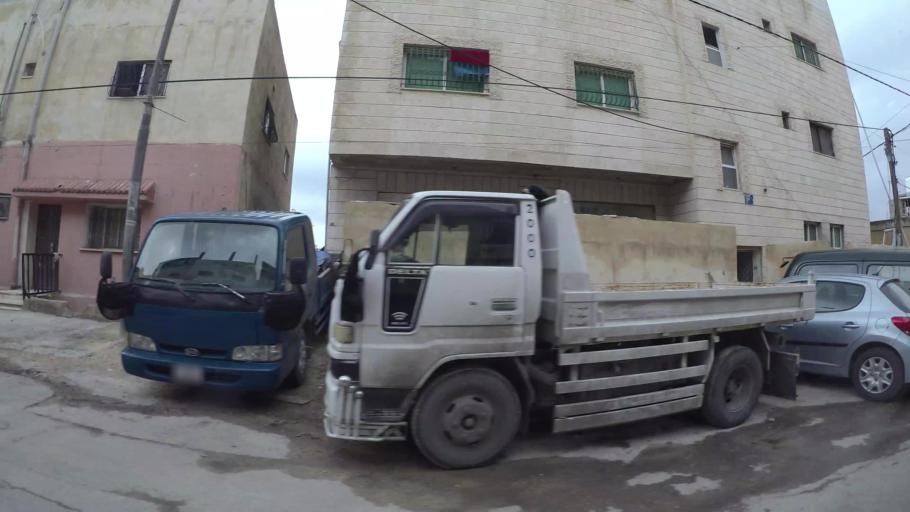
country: JO
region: Amman
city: Wadi as Sir
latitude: 31.9456
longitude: 35.8184
